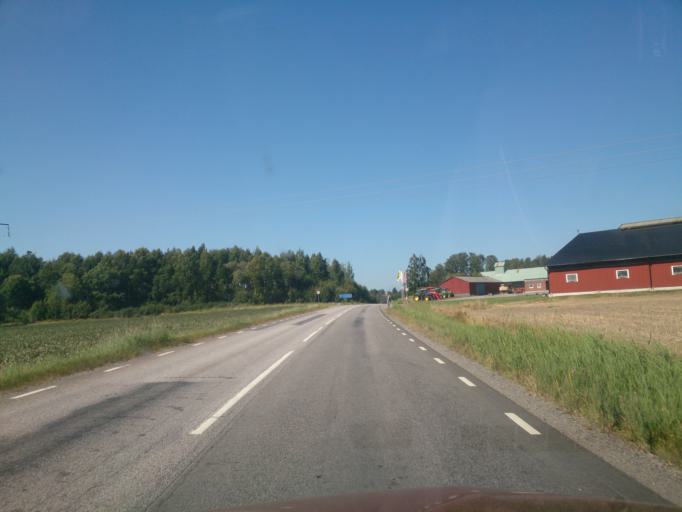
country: SE
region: OEstergoetland
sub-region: Norrkopings Kommun
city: Krokek
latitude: 58.5774
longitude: 16.3968
